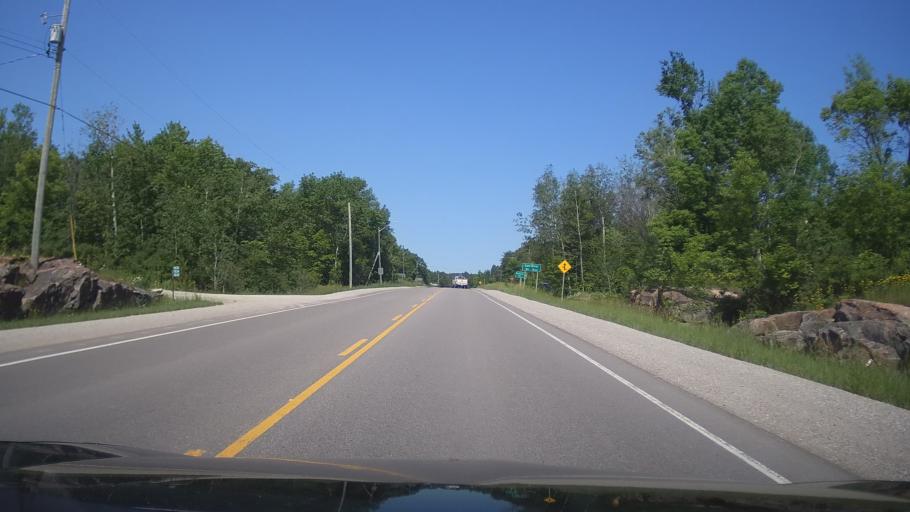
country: CA
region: Ontario
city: Orillia
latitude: 44.7427
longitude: -79.3084
